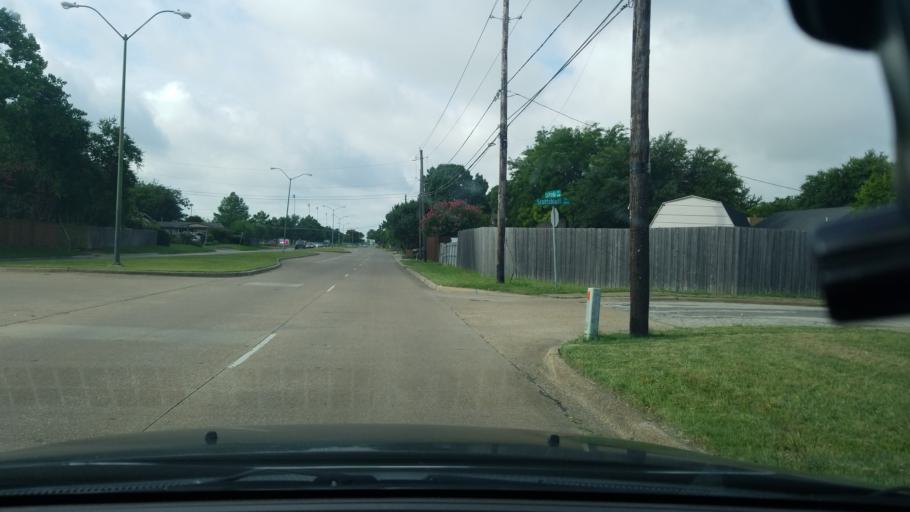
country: US
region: Texas
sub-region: Dallas County
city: Mesquite
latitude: 32.8171
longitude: -96.6655
